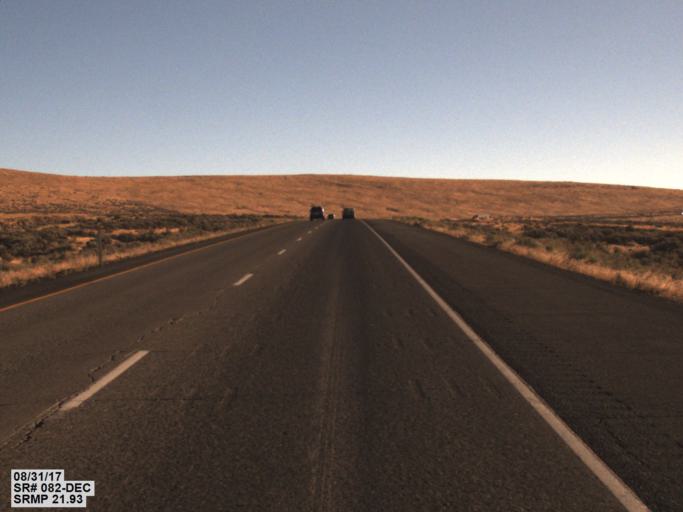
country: US
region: Washington
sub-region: Yakima County
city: Terrace Heights
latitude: 46.7173
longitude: -120.4096
